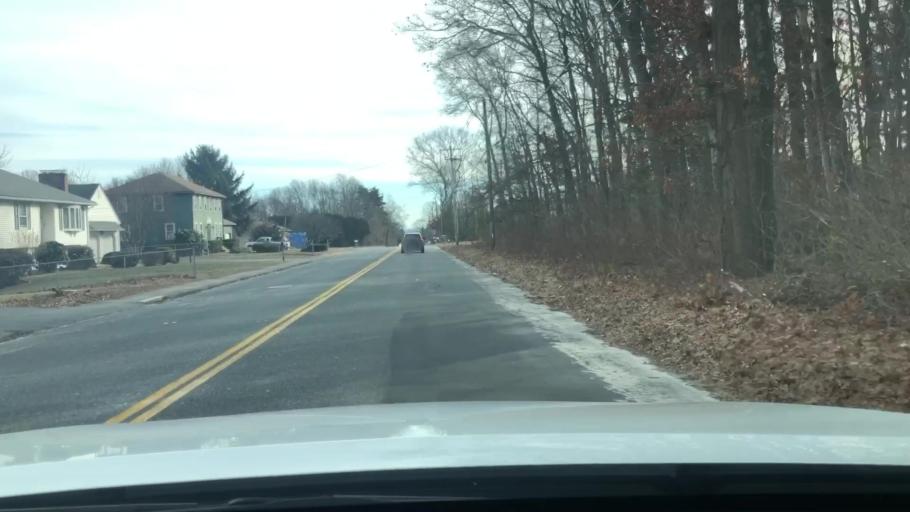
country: US
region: Massachusetts
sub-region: Worcester County
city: Hopedale
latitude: 42.1488
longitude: -71.5396
